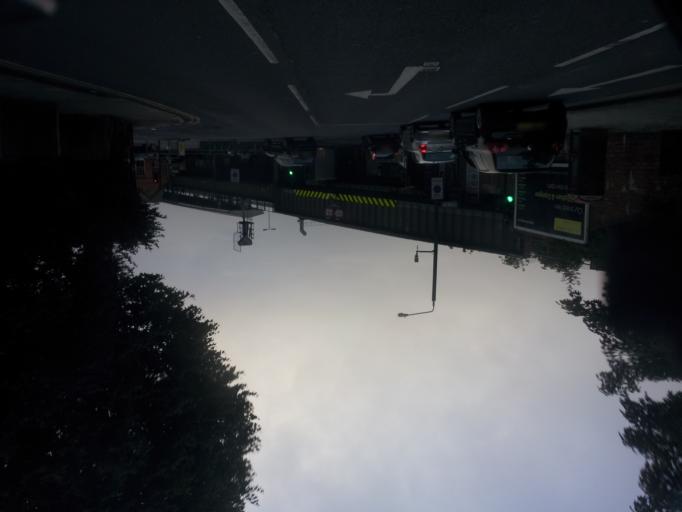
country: GB
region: England
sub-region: Greater London
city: Bromley
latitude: 51.4065
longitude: 0.0008
